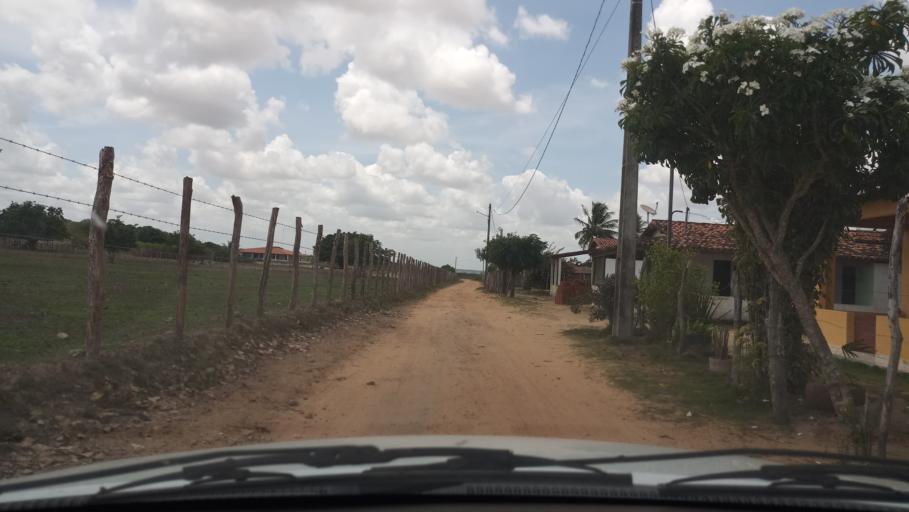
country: BR
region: Rio Grande do Norte
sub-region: Brejinho
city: Brejinho
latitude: -6.2747
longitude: -35.3473
